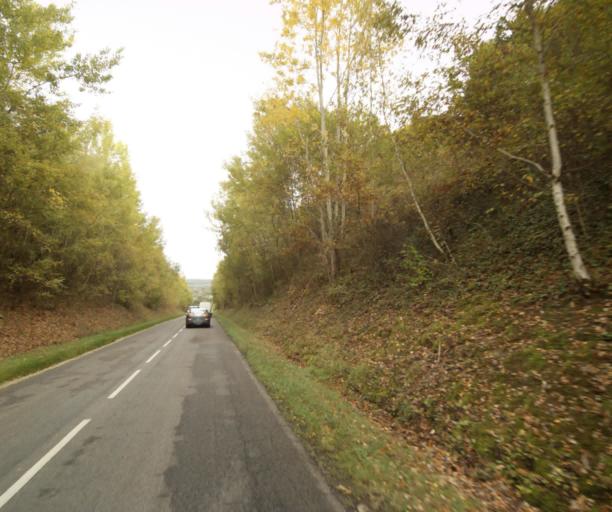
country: FR
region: Centre
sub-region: Departement d'Eure-et-Loir
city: Dreux
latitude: 48.7673
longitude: 1.3698
